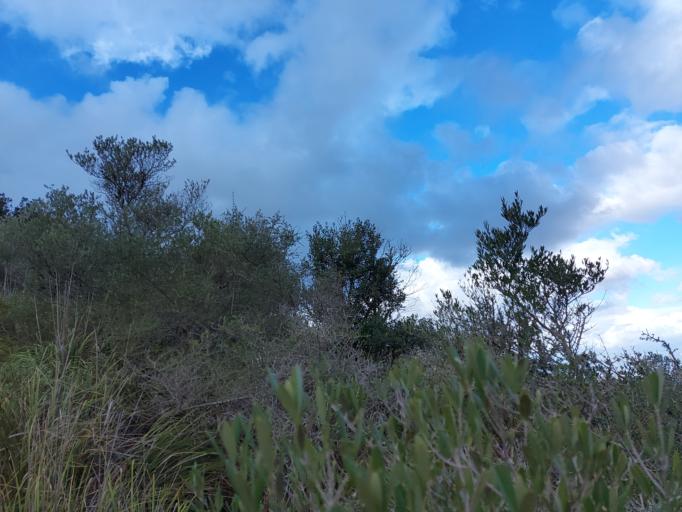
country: ES
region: Balearic Islands
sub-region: Illes Balears
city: Llucmajor
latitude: 39.5218
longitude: 2.9186
